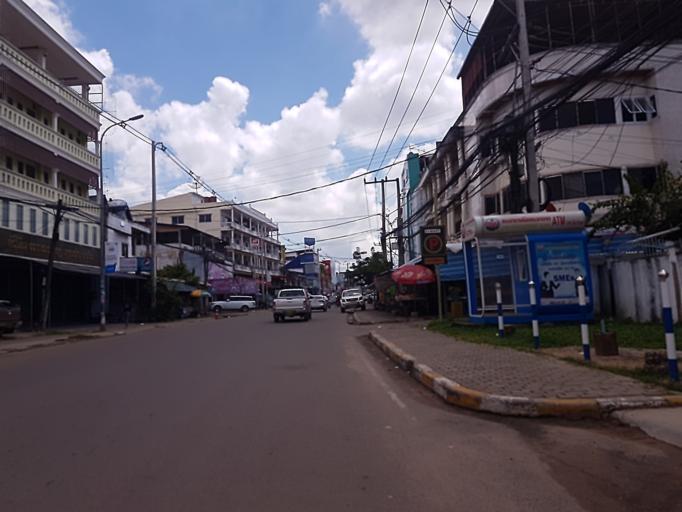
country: LA
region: Vientiane
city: Vientiane
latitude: 17.9628
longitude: 102.6215
